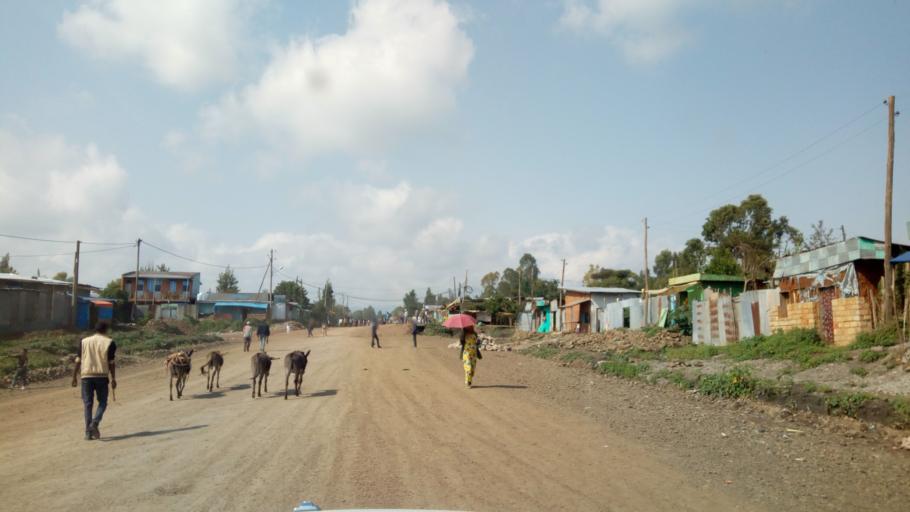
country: ET
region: Oromiya
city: Hagere Hiywet
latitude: 8.9768
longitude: 37.8518
